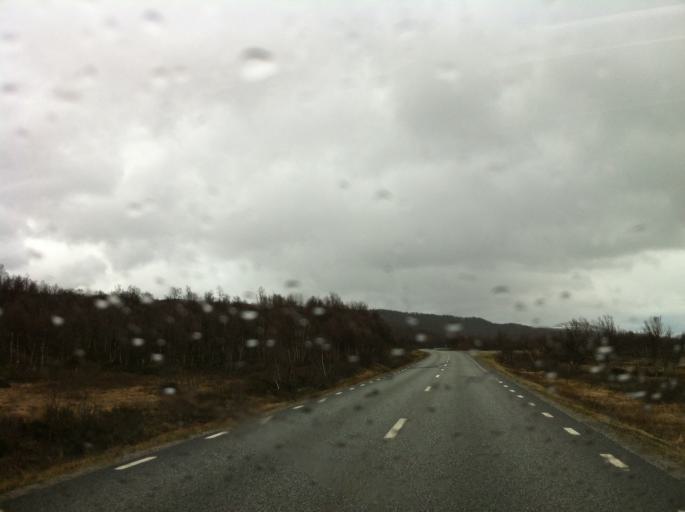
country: NO
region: Sor-Trondelag
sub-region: Tydal
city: Aas
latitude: 62.6300
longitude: 12.1232
